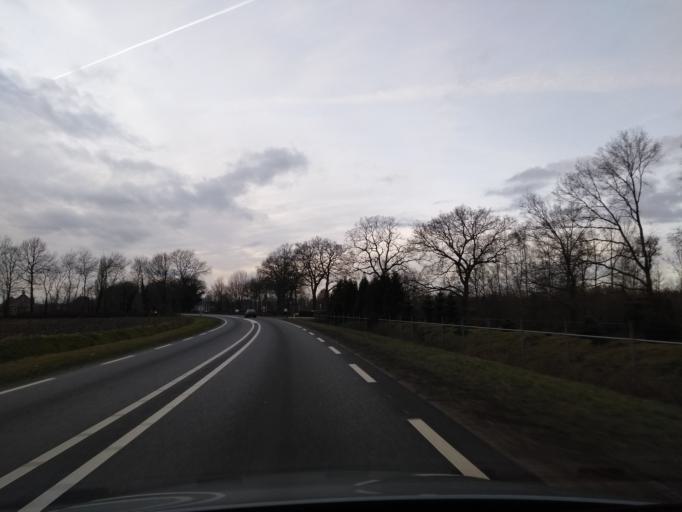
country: NL
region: Overijssel
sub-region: Gemeente Tubbergen
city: Tubbergen
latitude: 52.3649
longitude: 6.8403
